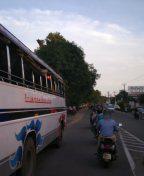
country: IN
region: Kerala
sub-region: Thrissur District
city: Trichur
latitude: 10.5426
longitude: 76.1847
